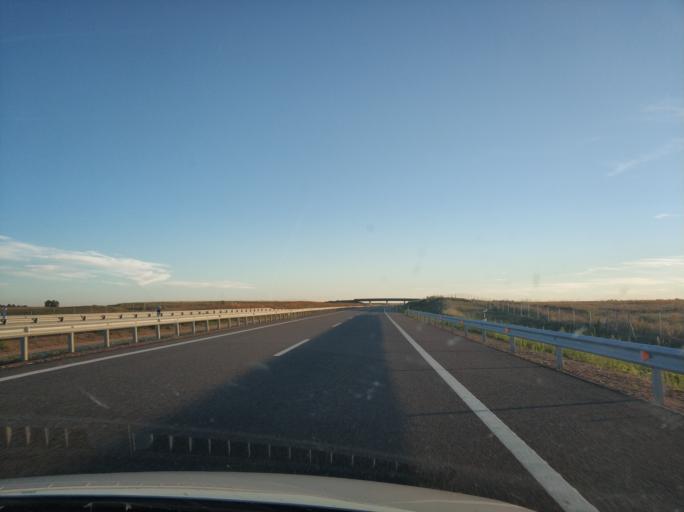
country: ES
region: Castille and Leon
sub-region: Provincia de Zamora
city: Castrogonzalo
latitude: 41.9570
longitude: -5.6156
